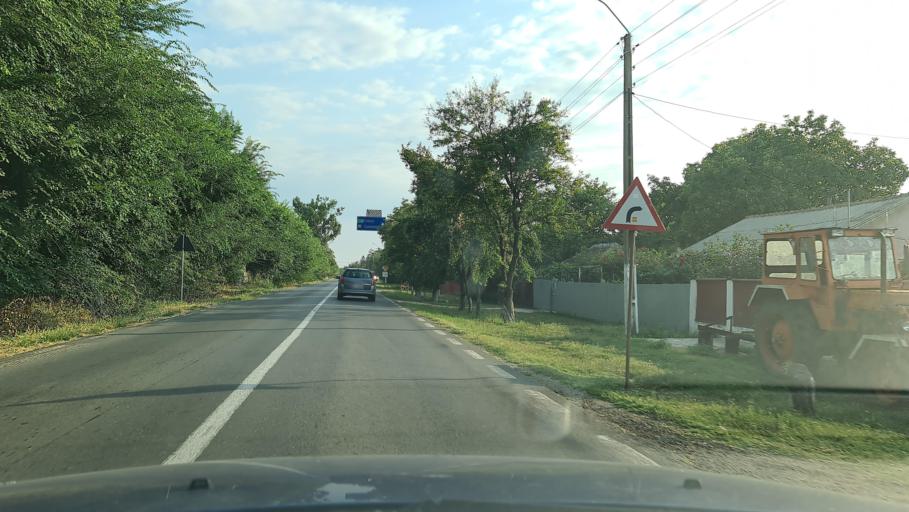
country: RO
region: Calarasi
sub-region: Comuna Dor Marunt
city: Dor Marunt
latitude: 44.4542
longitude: 26.9002
